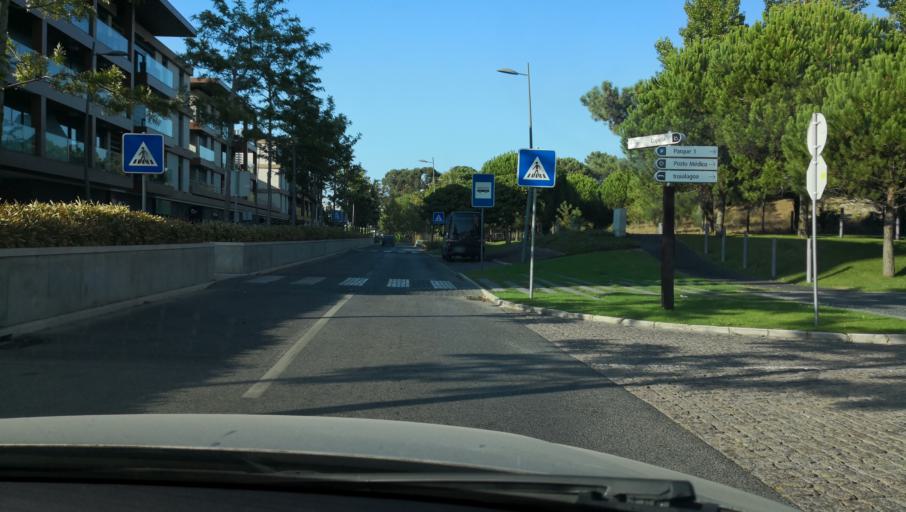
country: PT
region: Setubal
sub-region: Setubal
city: Setubal
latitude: 38.4906
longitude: -8.9012
